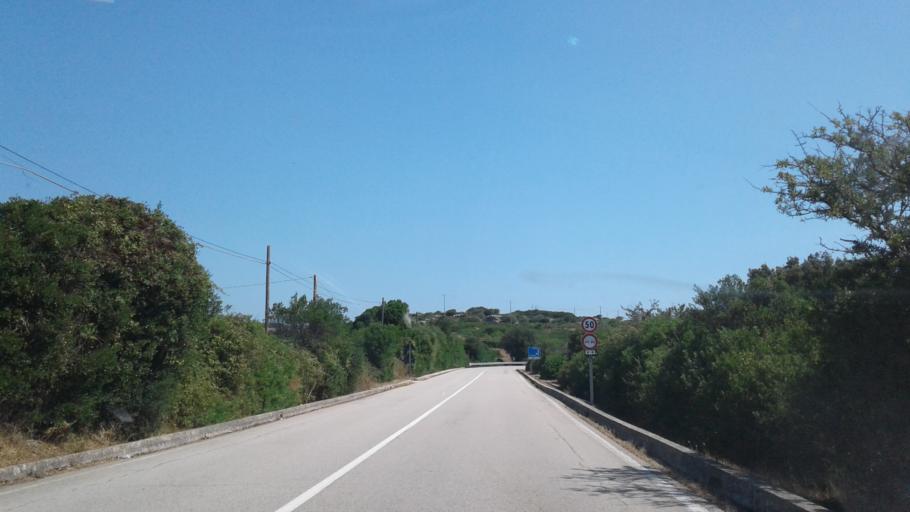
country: IT
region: Sardinia
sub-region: Provincia di Olbia-Tempio
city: Palau
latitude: 41.1275
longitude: 9.2848
